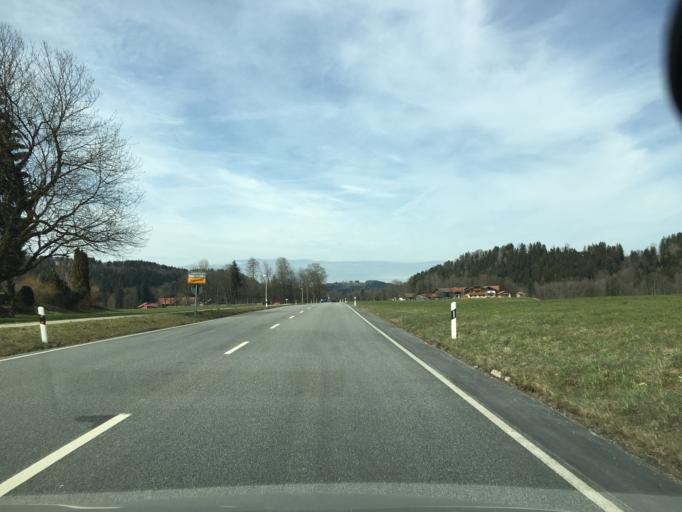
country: DE
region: Bavaria
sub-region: Upper Bavaria
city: Siegsdorf
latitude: 47.8030
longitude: 12.6972
